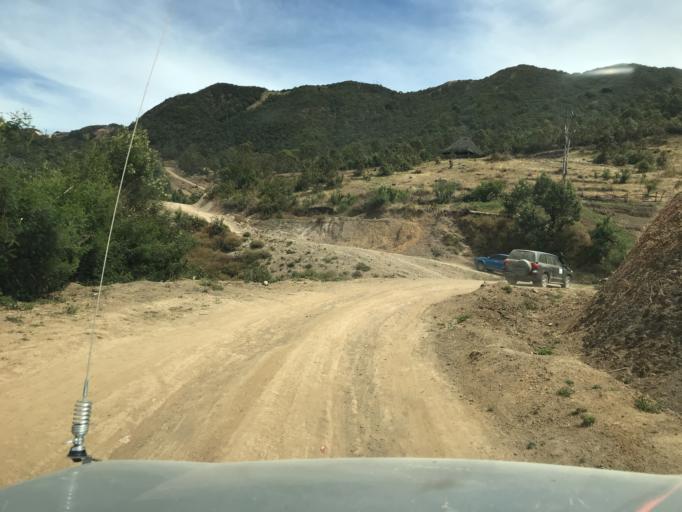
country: TL
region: Ainaro
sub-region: Ainaro
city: Ainaro
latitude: -8.8800
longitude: 125.5330
